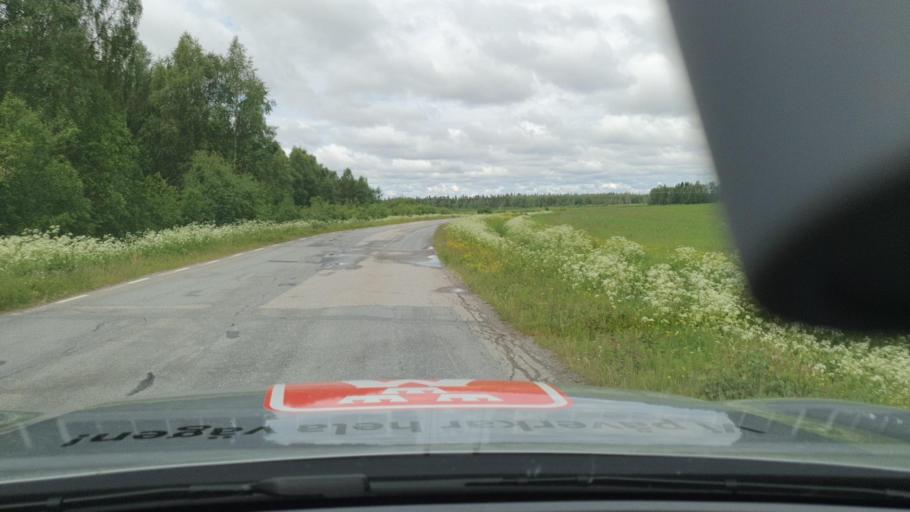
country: SE
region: Norrbotten
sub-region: Lulea Kommun
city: Ranea
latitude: 65.7759
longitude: 22.2290
